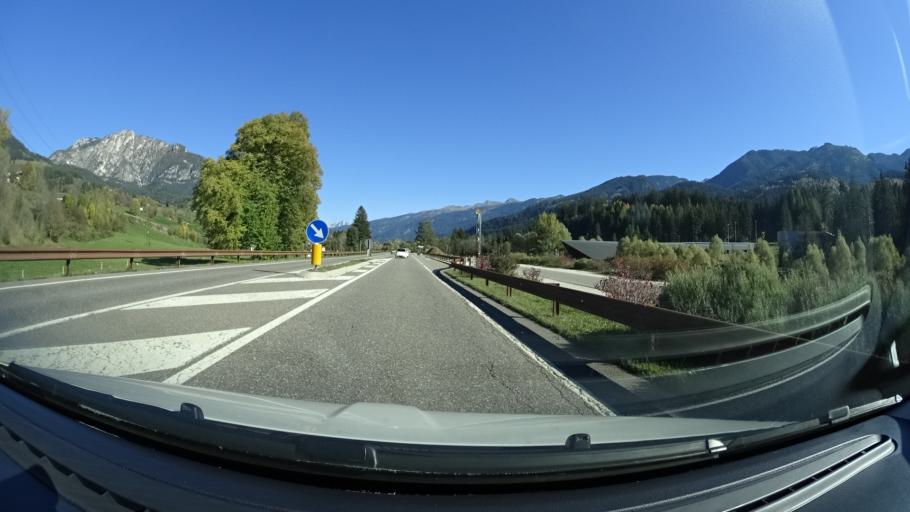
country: IT
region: Trentino-Alto Adige
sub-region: Provincia di Trento
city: Cavalese
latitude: 46.2846
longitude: 11.4697
